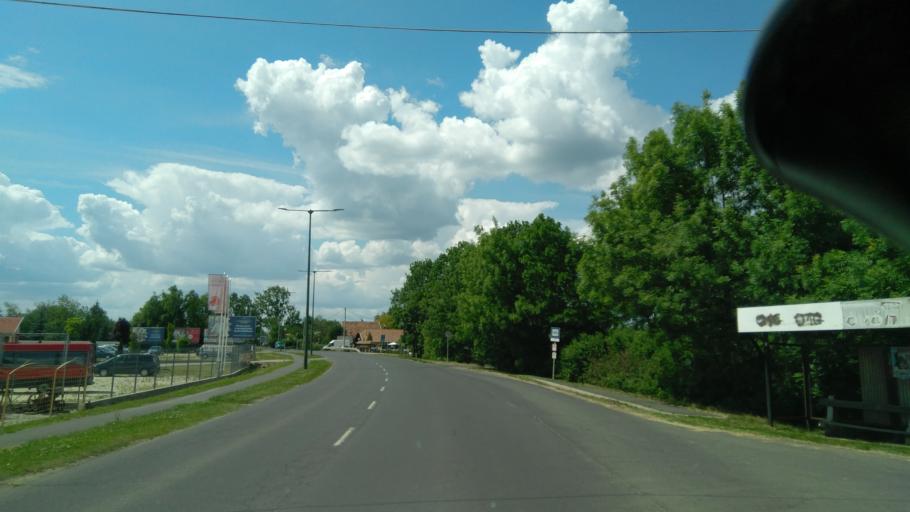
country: HU
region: Bekes
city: Gyula
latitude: 46.6519
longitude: 21.2457
